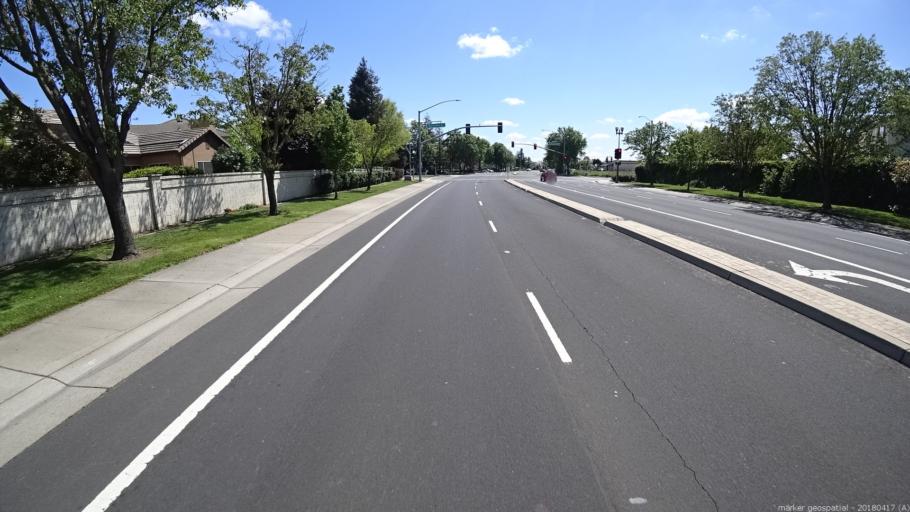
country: US
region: California
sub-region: Sacramento County
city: Laguna
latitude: 38.4112
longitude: -121.4772
